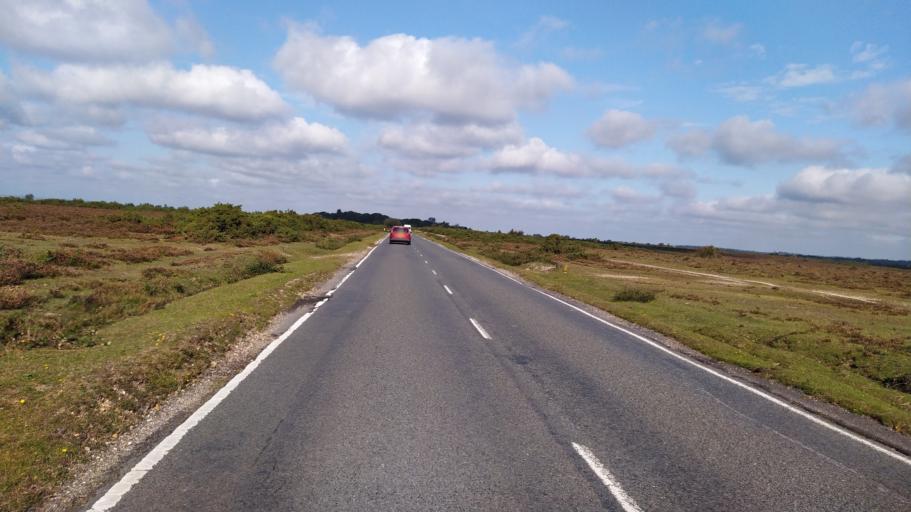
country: GB
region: England
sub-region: Hampshire
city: Bransgore
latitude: 50.8469
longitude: -1.7246
